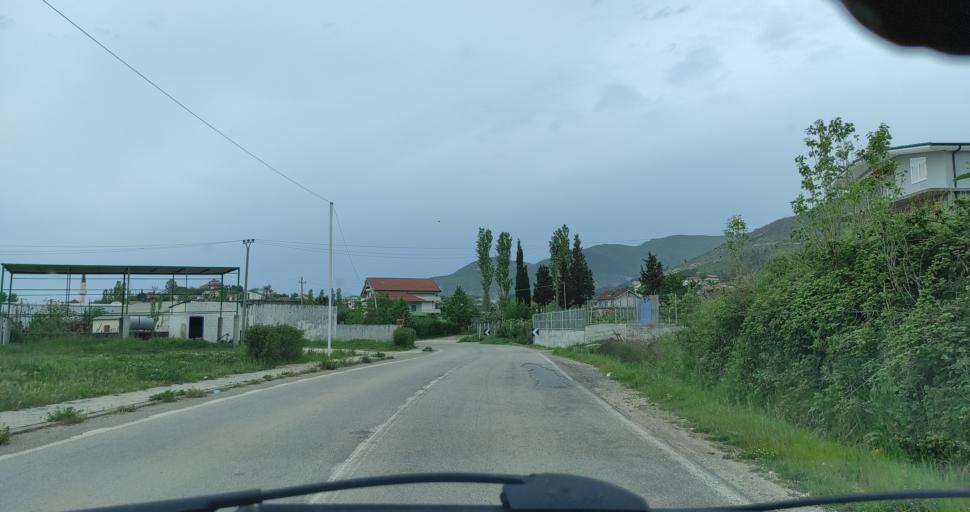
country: AL
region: Lezhe
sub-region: Rrethi i Kurbinit
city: Lac
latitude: 41.6175
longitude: 19.7114
